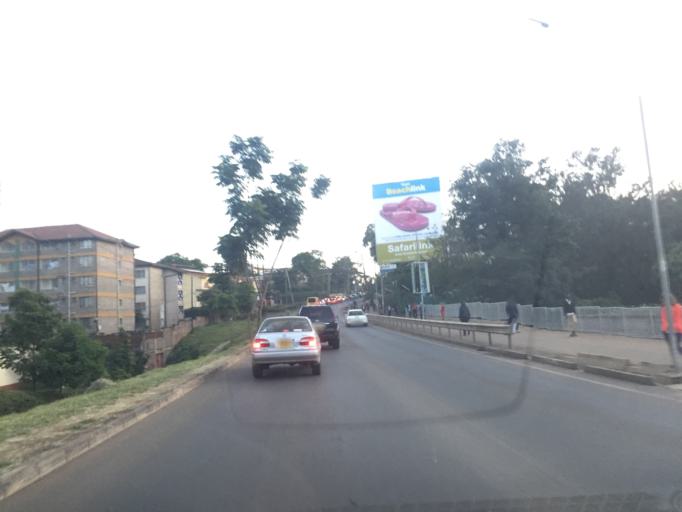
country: KE
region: Nairobi Area
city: Nairobi
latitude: -1.2688
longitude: 36.8017
